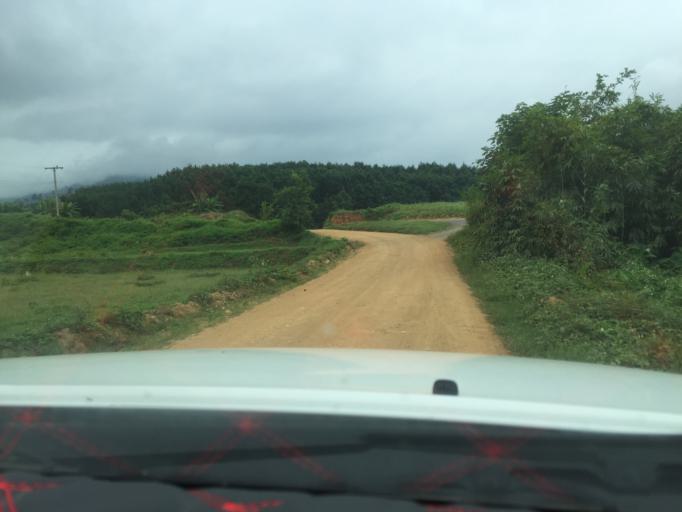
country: TH
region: Phayao
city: Phu Sang
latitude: 19.6938
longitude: 100.5012
